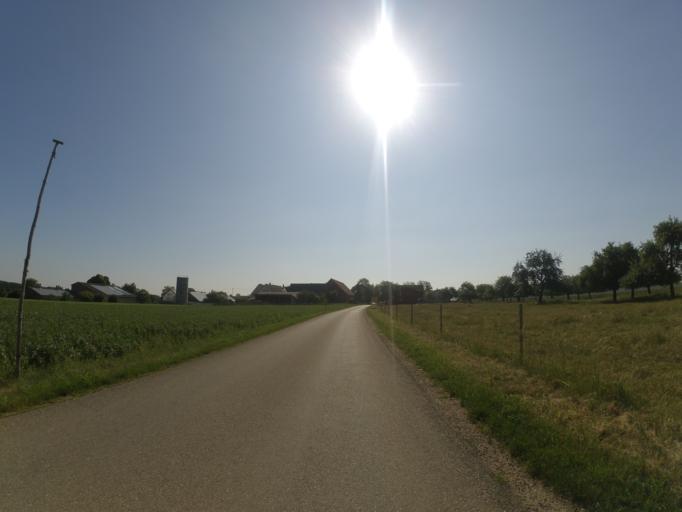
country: DE
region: Baden-Wuerttemberg
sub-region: Tuebingen Region
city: Beimerstetten
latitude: 48.4692
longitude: 9.9900
